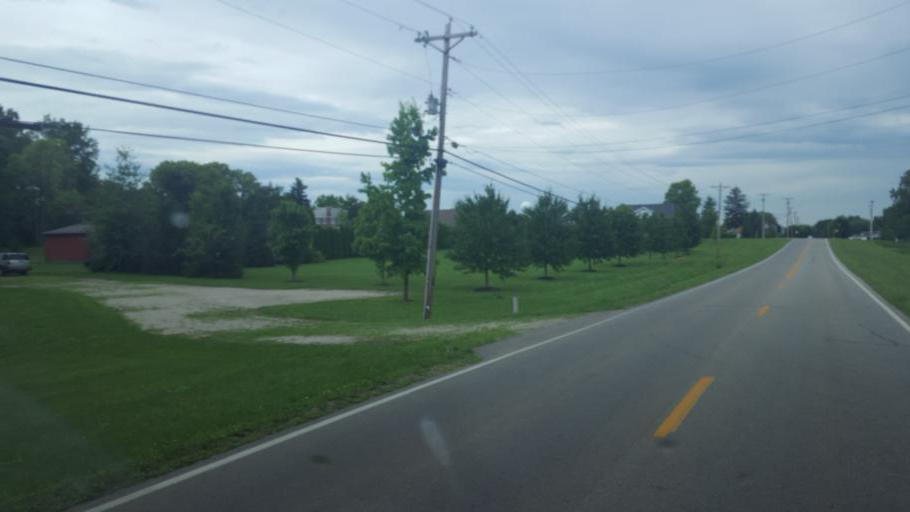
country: US
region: Ohio
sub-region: Pickaway County
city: Ashville
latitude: 39.7123
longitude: -82.9442
